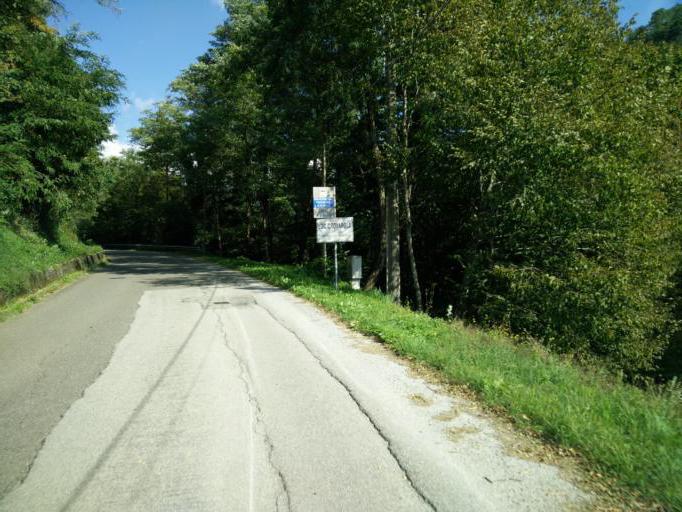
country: IT
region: Liguria
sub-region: Provincia di La Spezia
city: Sesta Godano
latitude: 44.2992
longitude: 9.6803
